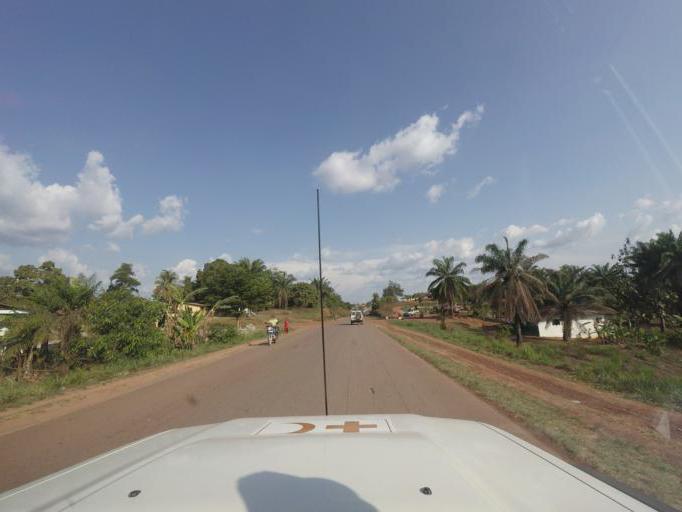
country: LR
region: Bong
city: Gbarnga
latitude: 7.0096
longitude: -9.4820
